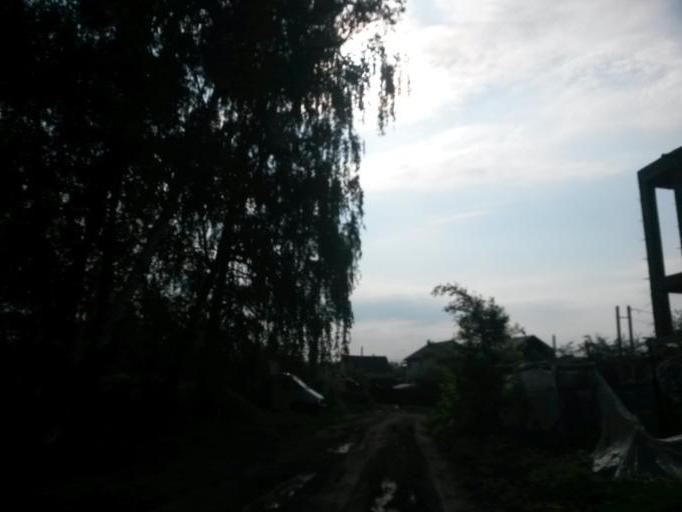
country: RU
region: Moscow
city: Zyablikovo
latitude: 55.5943
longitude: 37.7672
